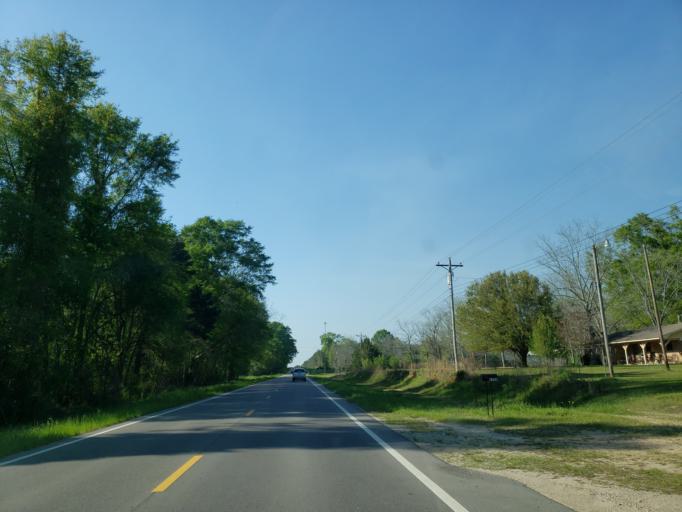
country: US
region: Mississippi
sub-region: Perry County
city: Richton
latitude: 31.4121
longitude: -88.9543
